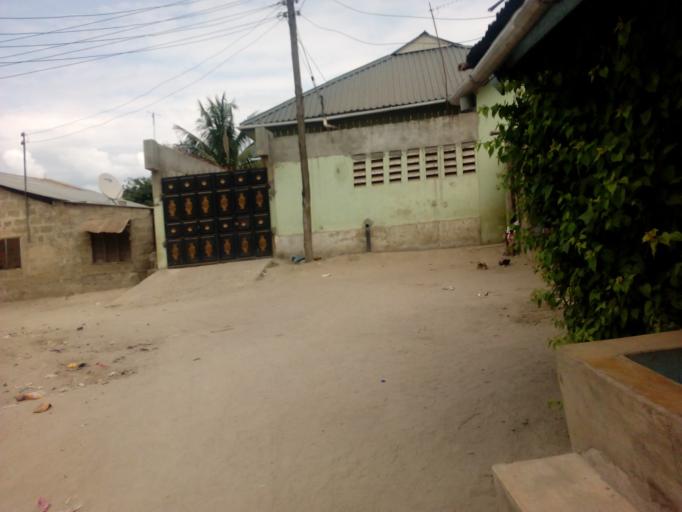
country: TZ
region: Dar es Salaam
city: Dar es Salaam
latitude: -6.8584
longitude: 39.2537
